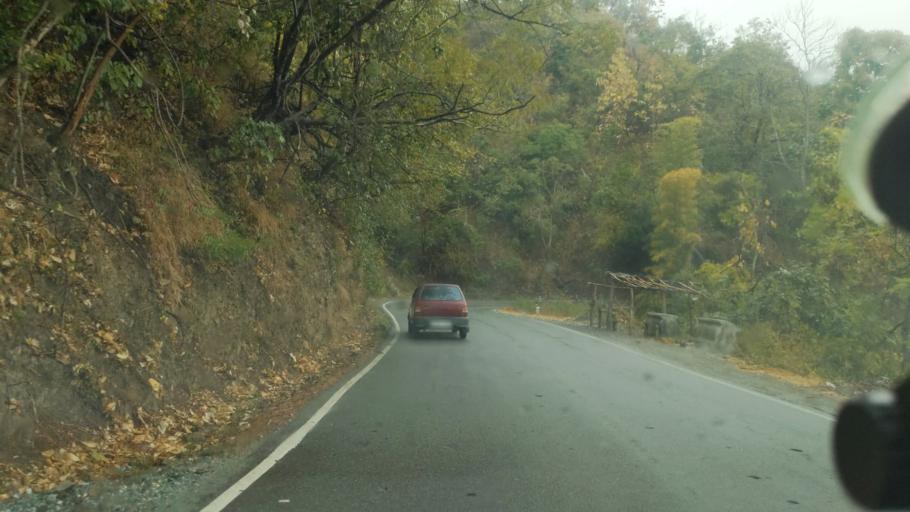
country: IN
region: Uttarakhand
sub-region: Naini Tal
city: Bhim Tal
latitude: 29.3012
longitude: 79.5577
